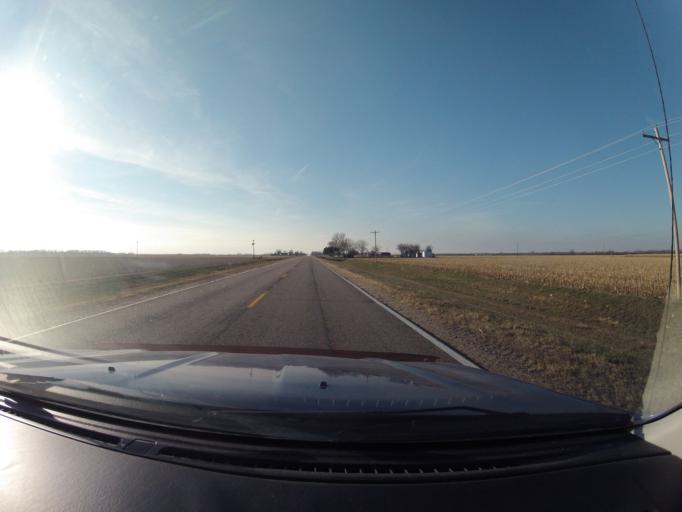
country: US
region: Nebraska
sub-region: Buffalo County
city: Kearney
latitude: 40.6410
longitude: -98.9780
